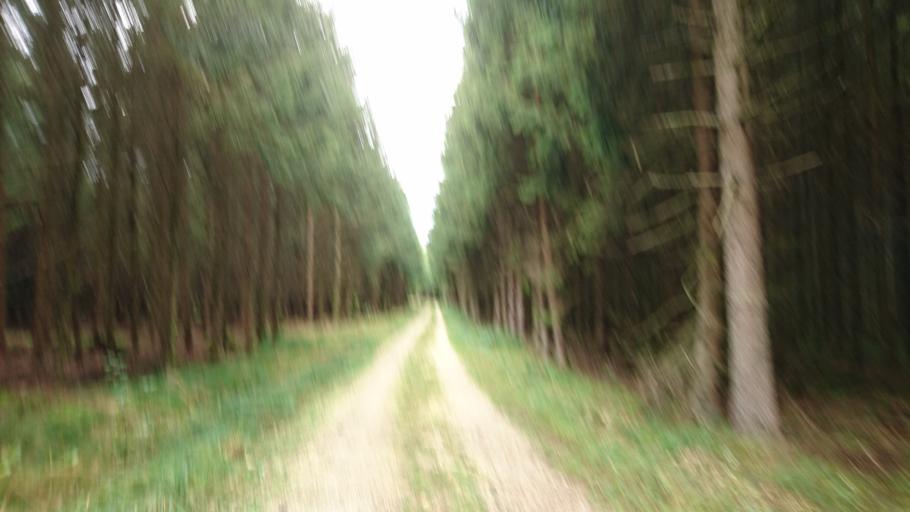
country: DE
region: Bavaria
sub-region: Swabia
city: Welden
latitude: 48.4376
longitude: 10.6327
